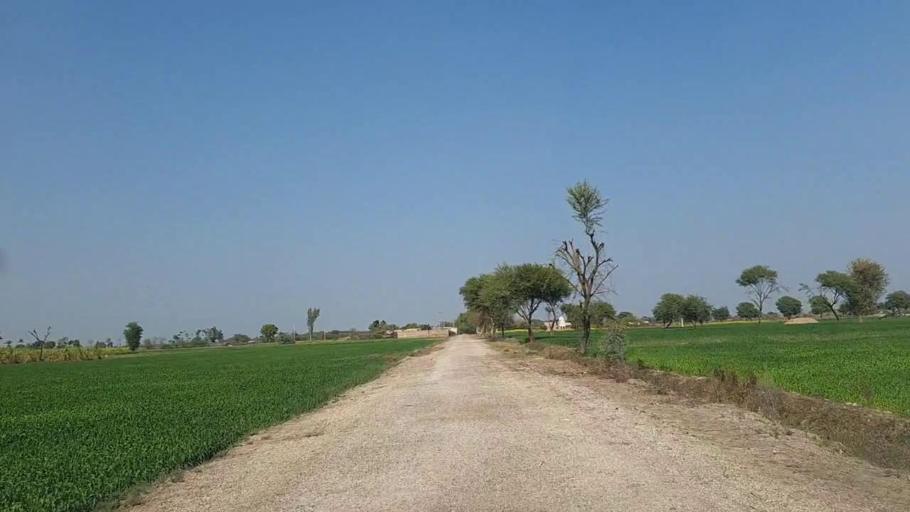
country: PK
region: Sindh
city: Jam Sahib
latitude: 26.2705
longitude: 68.5210
